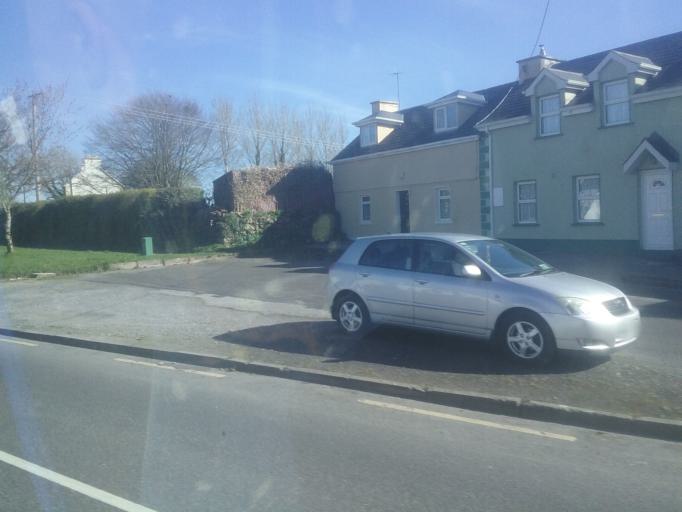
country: IE
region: Munster
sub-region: An Clar
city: Ennis
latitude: 52.9453
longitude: -9.0624
